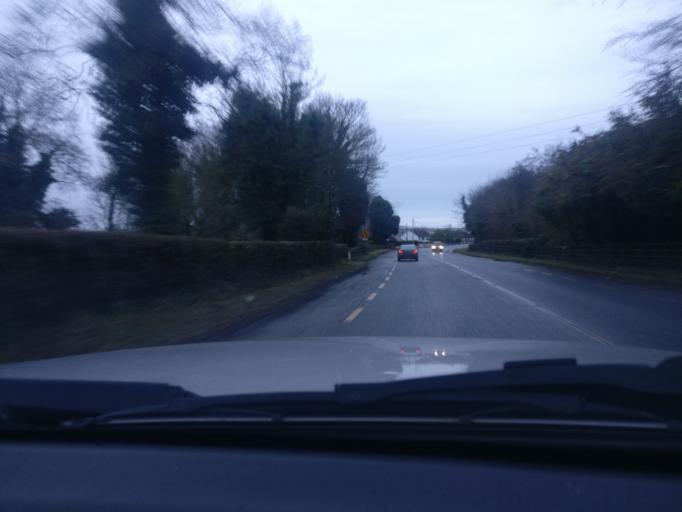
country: IE
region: Leinster
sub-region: An Mhi
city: Navan
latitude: 53.6566
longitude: -6.7071
